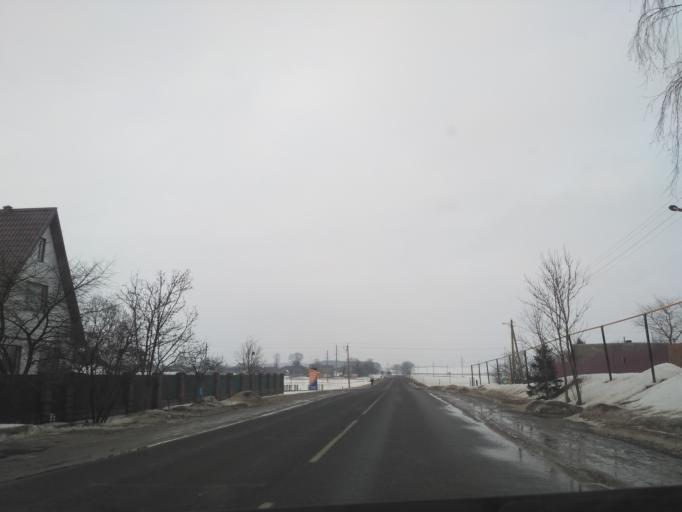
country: BY
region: Minsk
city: Horad Smalyavichy
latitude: 54.0282
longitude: 28.0621
